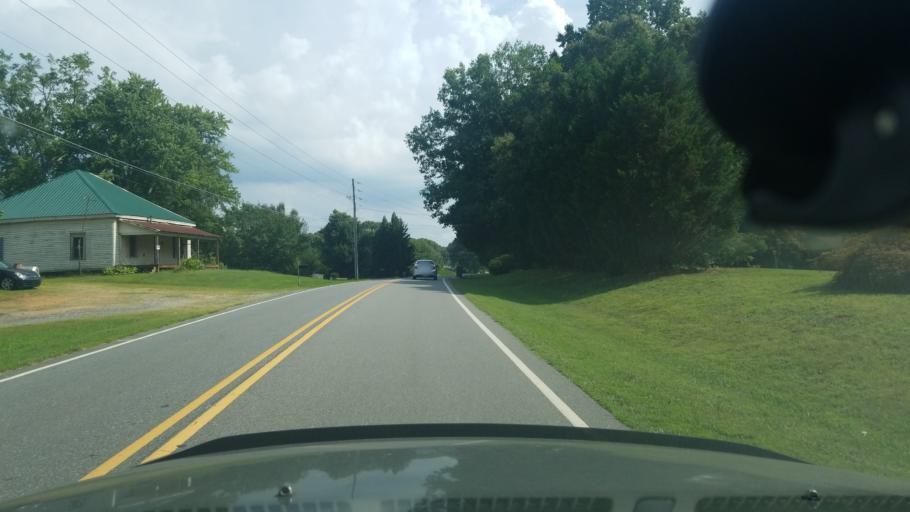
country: US
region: Georgia
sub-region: Hall County
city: Flowery Branch
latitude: 34.2596
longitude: -83.9954
